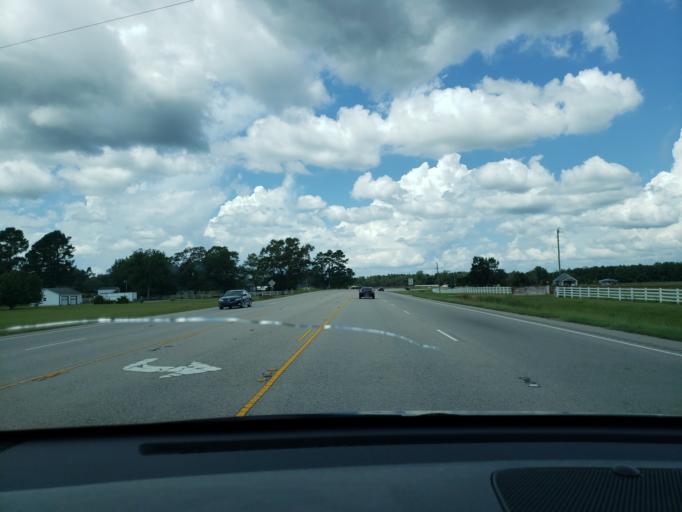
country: US
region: North Carolina
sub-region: Bladen County
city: Elizabethtown
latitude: 34.6723
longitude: -78.7370
